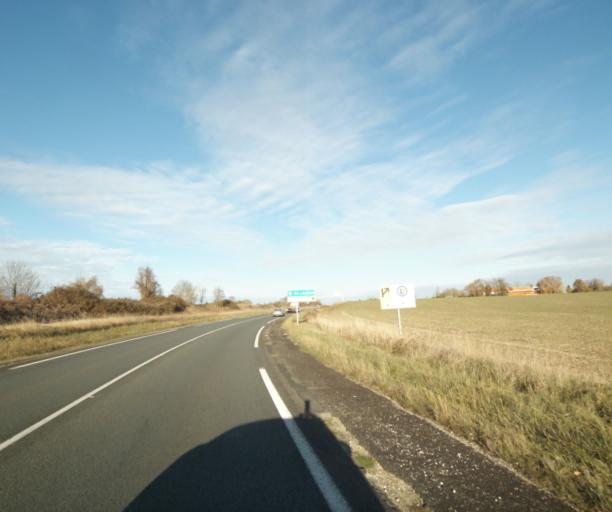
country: FR
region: Poitou-Charentes
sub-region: Departement de la Charente-Maritime
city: Saintes
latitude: 45.7414
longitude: -0.6713
